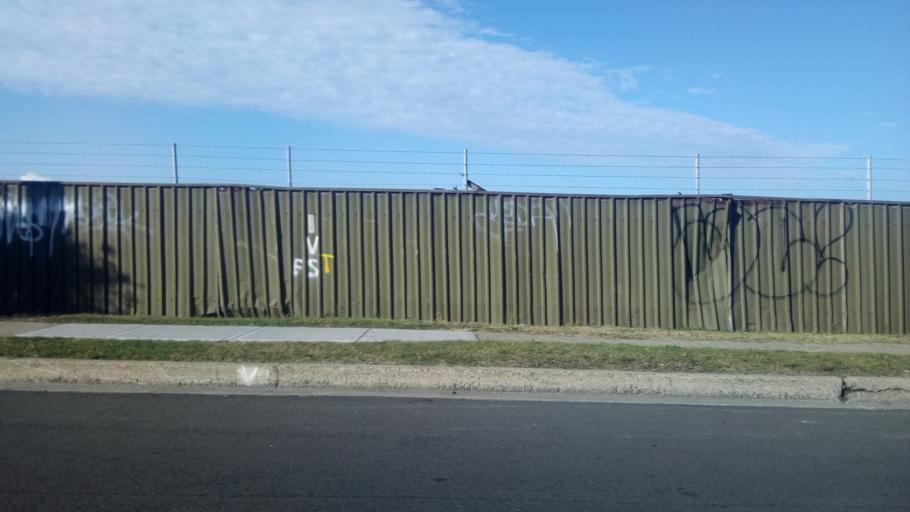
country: AU
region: New South Wales
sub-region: Wollongong
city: Port Kembla
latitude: -34.4790
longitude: 150.9085
